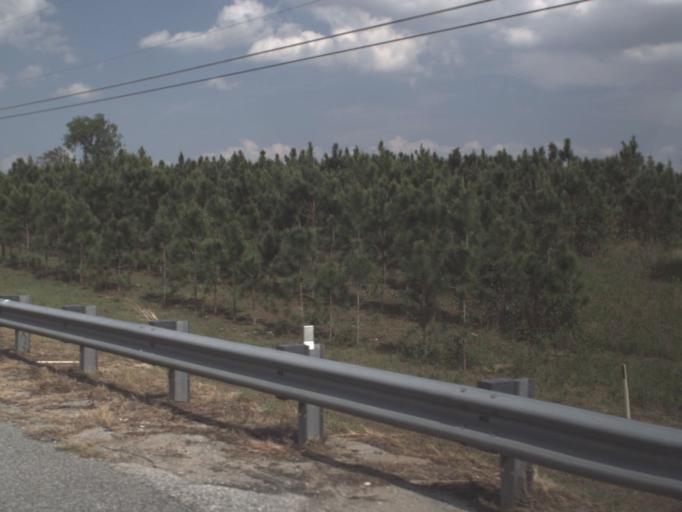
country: US
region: Florida
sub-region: Lake County
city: Howie In The Hills
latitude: 28.7287
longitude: -81.7733
